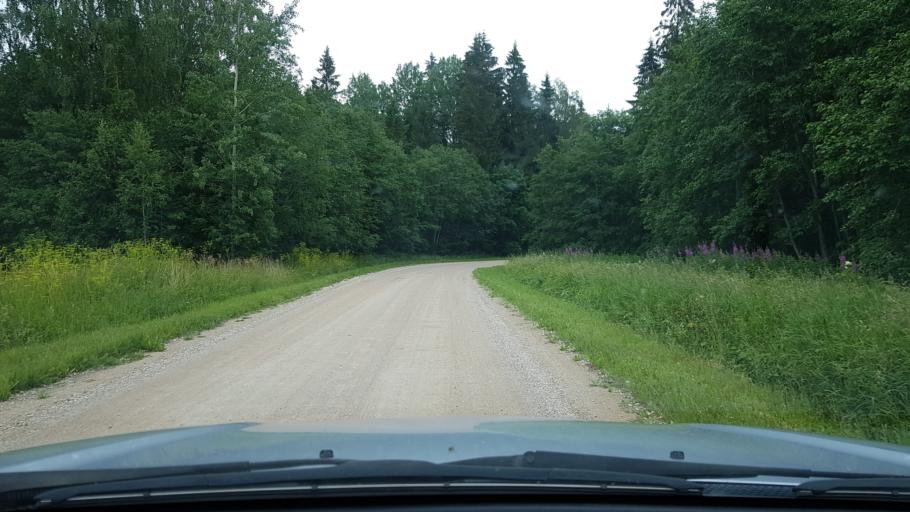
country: EE
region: Ida-Virumaa
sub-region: Narva-Joesuu linn
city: Narva-Joesuu
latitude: 59.3607
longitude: 28.0459
